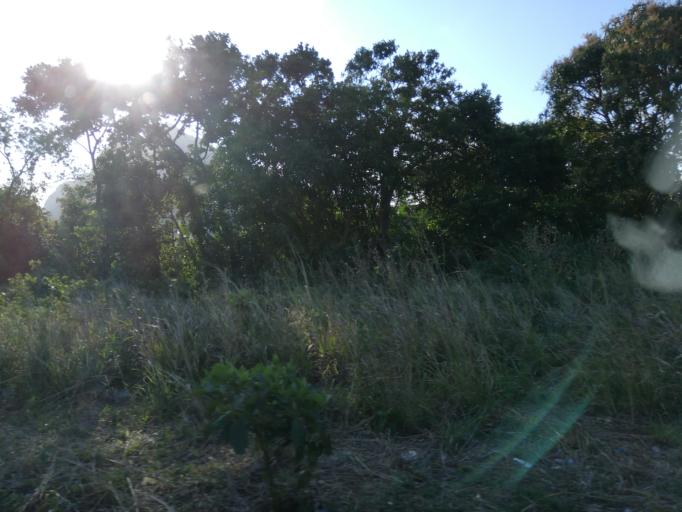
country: MU
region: Moka
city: Saint Pierre
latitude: -20.2147
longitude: 57.5252
